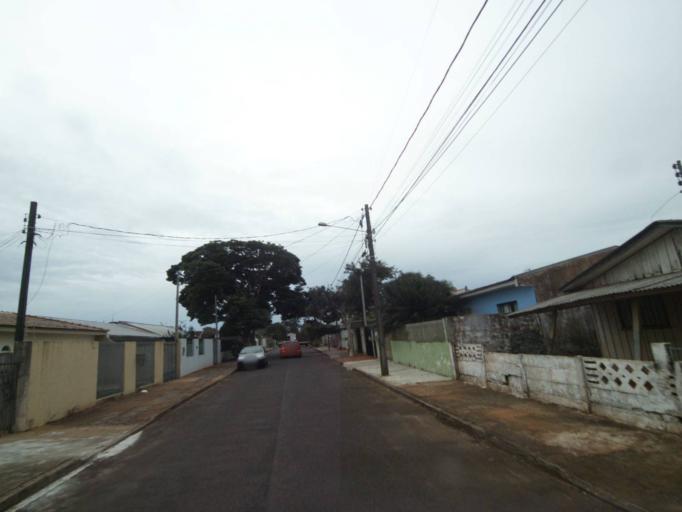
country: BR
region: Parana
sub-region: Campo Mourao
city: Campo Mourao
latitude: -24.0274
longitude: -52.3610
